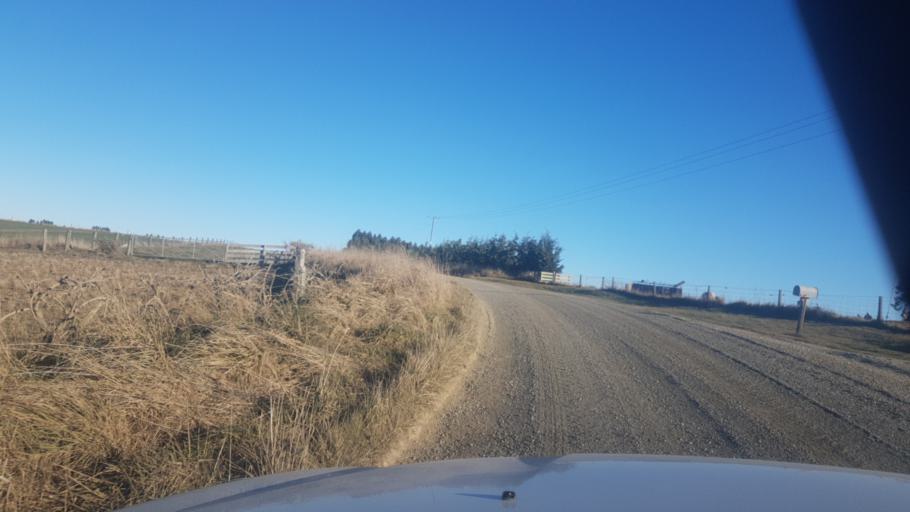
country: NZ
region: Canterbury
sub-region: Timaru District
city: Pleasant Point
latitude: -44.3474
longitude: 171.0746
